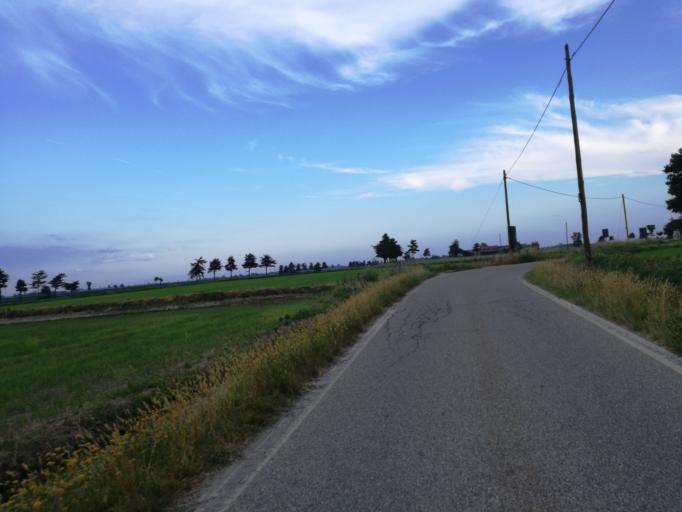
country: IT
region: Piedmont
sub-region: Provincia di Novara
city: Torrion Quartara
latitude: 45.3811
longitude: 8.6163
